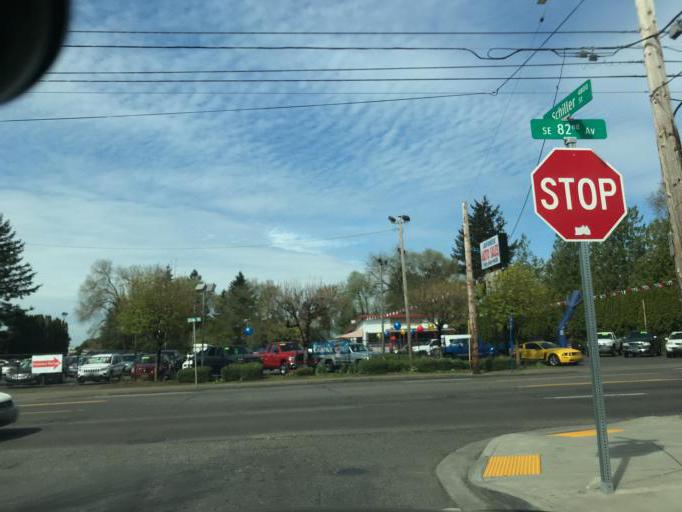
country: US
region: Oregon
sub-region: Multnomah County
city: Lents
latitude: 45.4880
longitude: -122.5786
